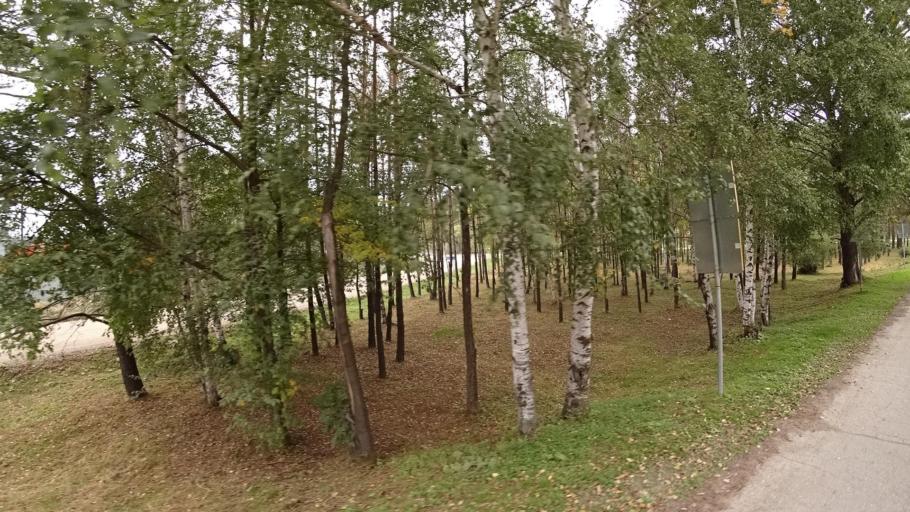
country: RU
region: Jewish Autonomous Oblast
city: Khingansk
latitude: 48.9865
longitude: 131.0600
